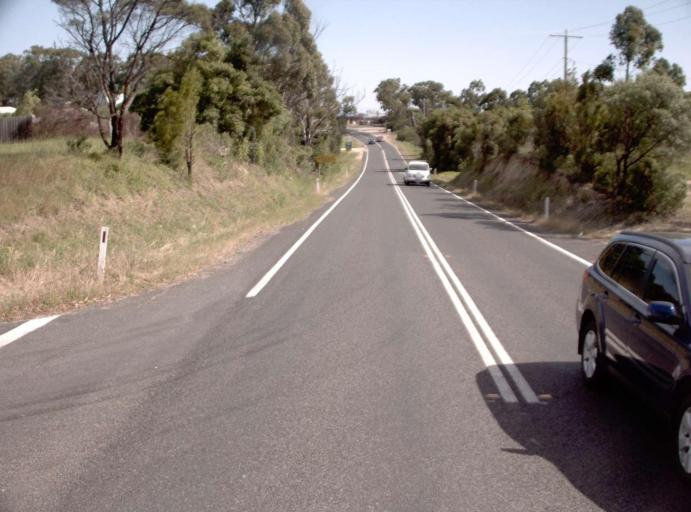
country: AU
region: Victoria
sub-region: East Gippsland
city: Lakes Entrance
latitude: -37.8753
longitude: 147.9615
